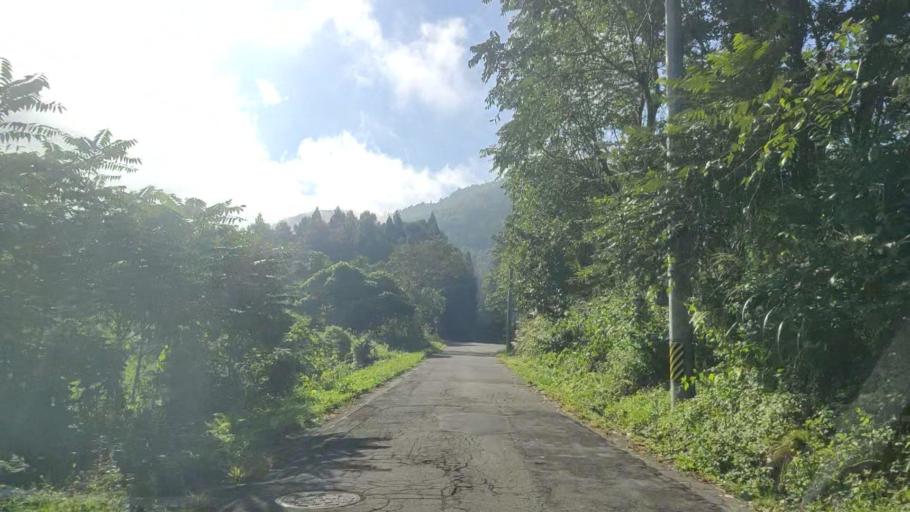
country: JP
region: Nagano
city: Iiyama
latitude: 36.8263
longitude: 138.4078
